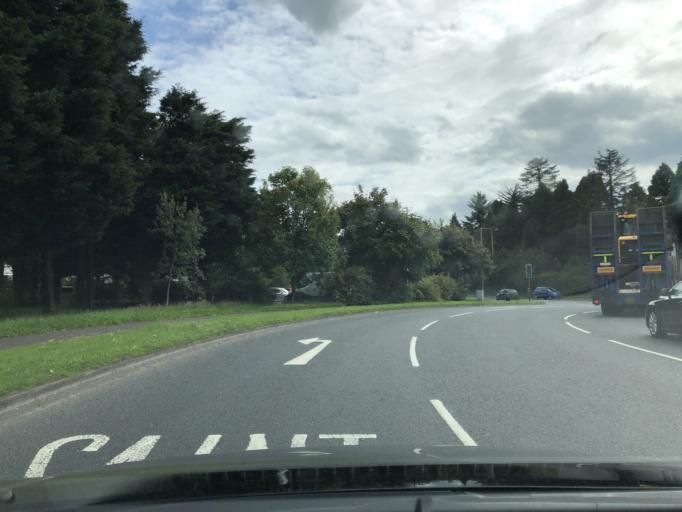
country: GB
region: Northern Ireland
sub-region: Lisburn District
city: Lisburn
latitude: 54.5058
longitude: -6.0277
